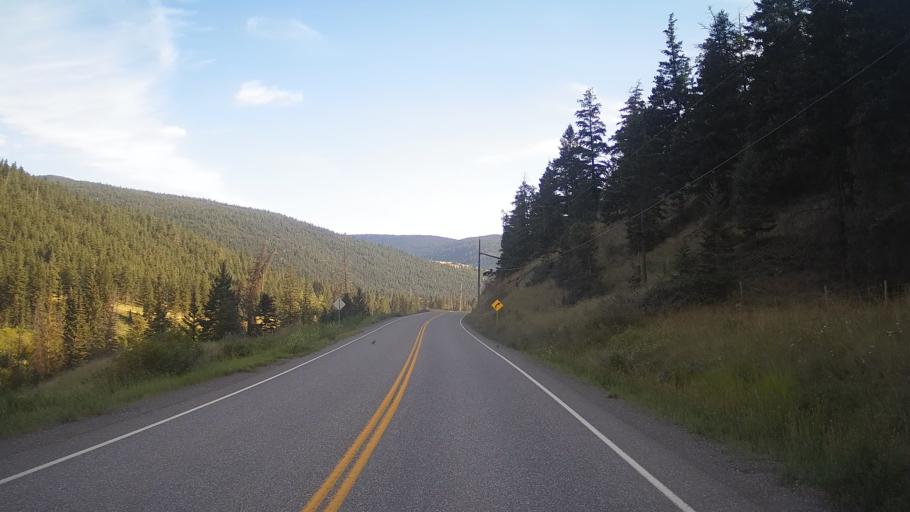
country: CA
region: British Columbia
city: Cache Creek
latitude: 50.8587
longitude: -121.5308
